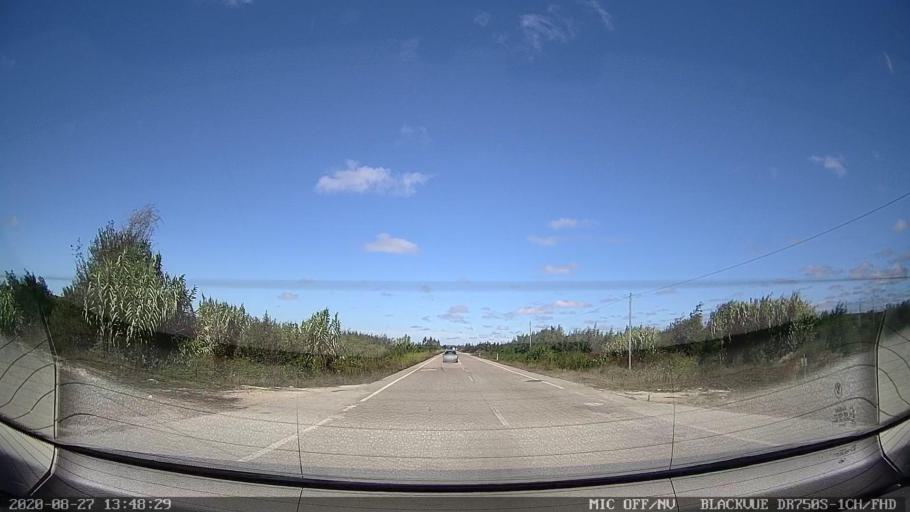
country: PT
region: Coimbra
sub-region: Mira
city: Mira
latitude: 40.3772
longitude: -8.7449
